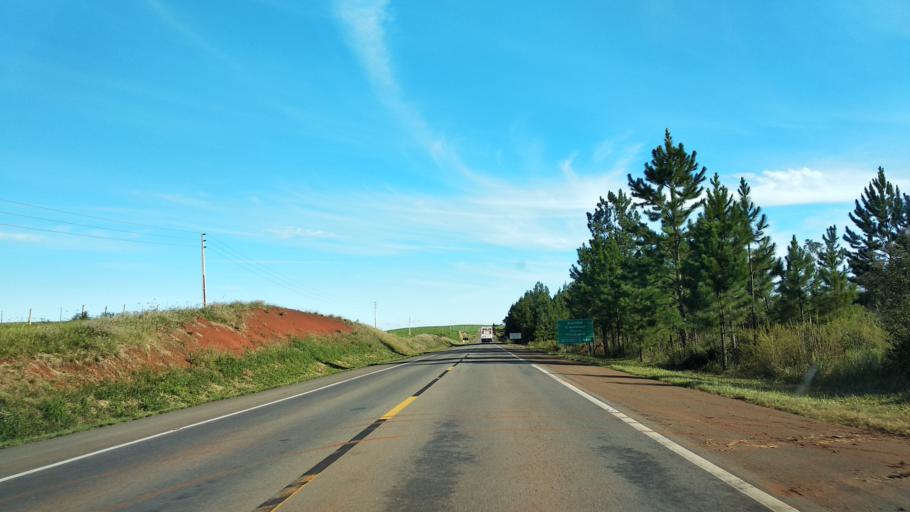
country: BR
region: Santa Catarina
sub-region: Celso Ramos
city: Celso Ramos
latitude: -27.5097
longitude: -51.3466
